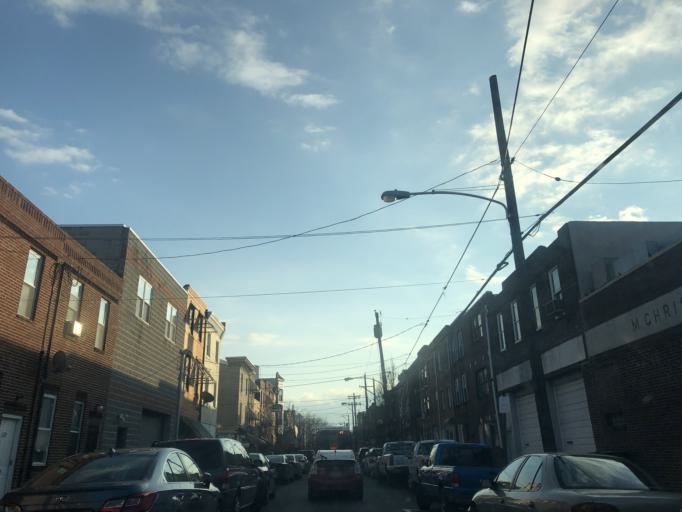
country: US
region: Pennsylvania
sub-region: Philadelphia County
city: Philadelphia
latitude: 39.9349
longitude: -75.1571
